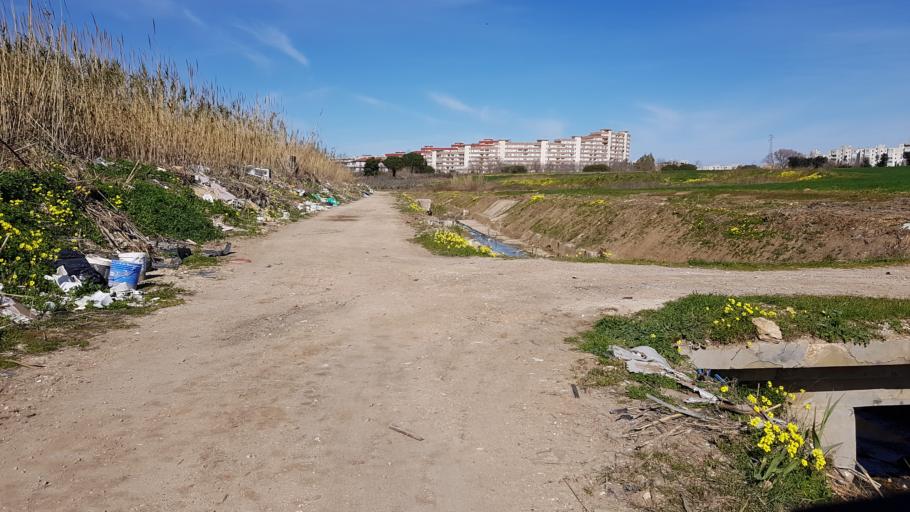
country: IT
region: Apulia
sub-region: Provincia di Brindisi
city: Brindisi
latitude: 40.6160
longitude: 17.9385
